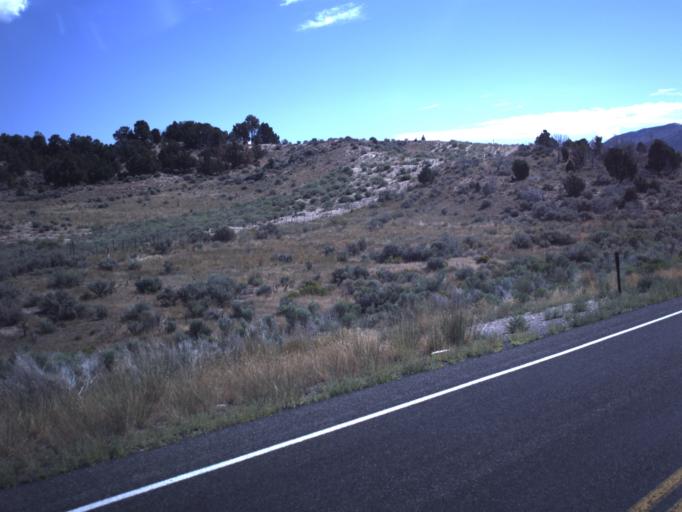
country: US
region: Utah
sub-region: Utah County
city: Genola
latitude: 39.9452
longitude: -112.2282
